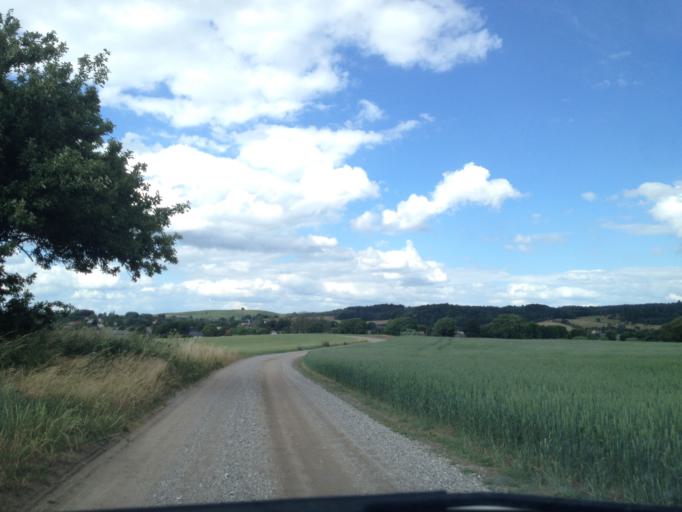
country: DK
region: Central Jutland
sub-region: Syddjurs Kommune
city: Ronde
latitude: 56.2010
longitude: 10.4833
